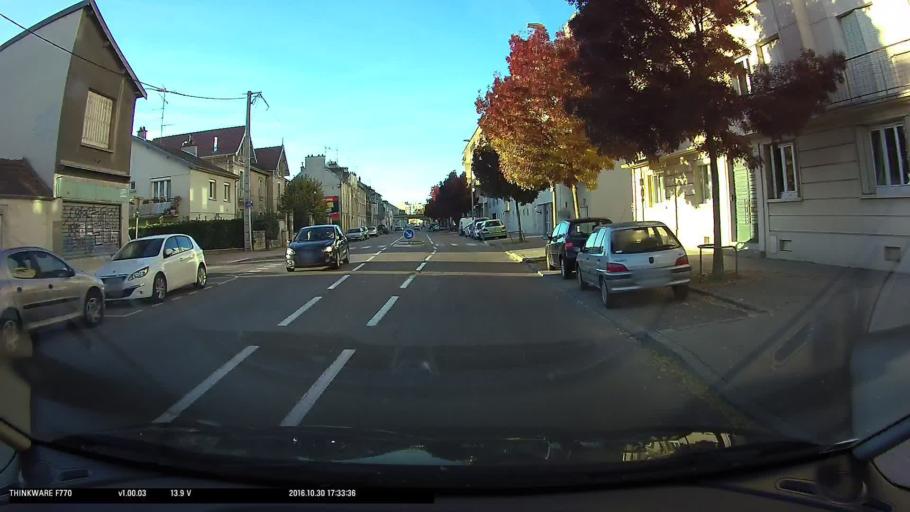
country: FR
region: Bourgogne
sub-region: Departement de la Cote-d'Or
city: Longvic
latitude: 47.3096
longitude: 5.0547
